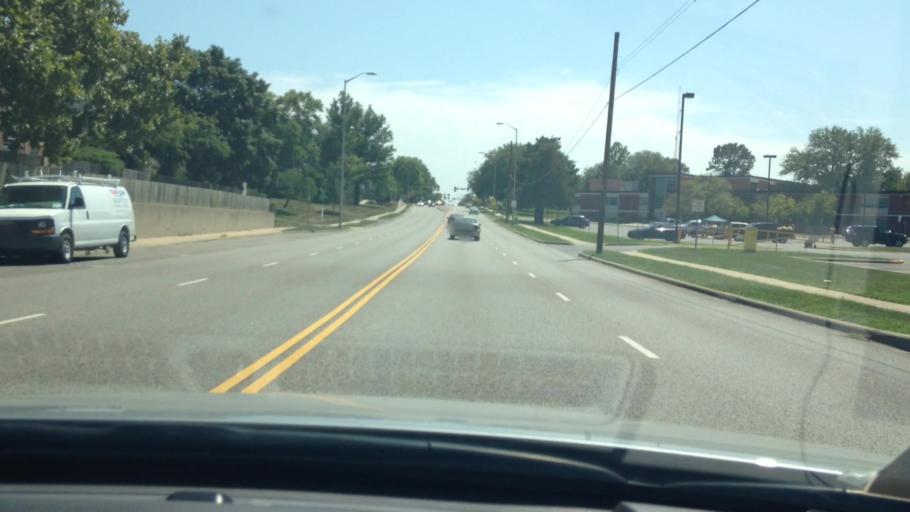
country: US
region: Kansas
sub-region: Johnson County
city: Overland Park
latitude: 38.9776
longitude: -94.6864
